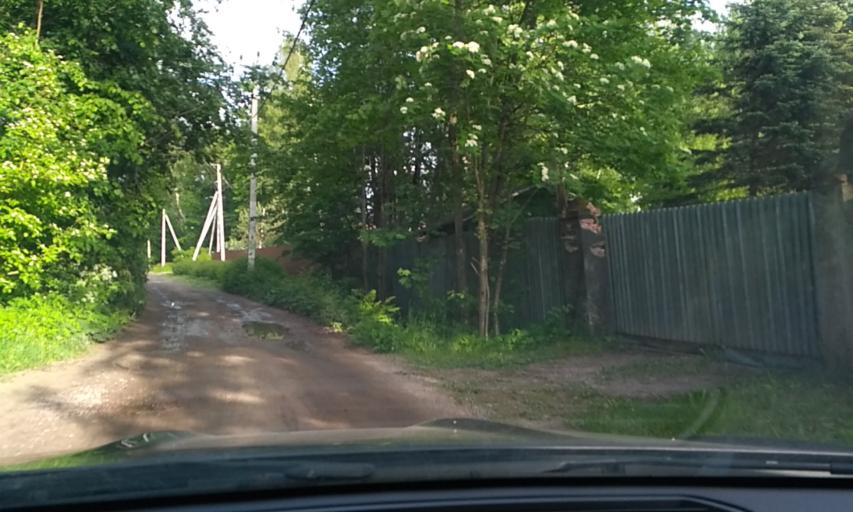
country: RU
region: Leningrad
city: Otradnoye
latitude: 59.8065
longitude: 30.8140
